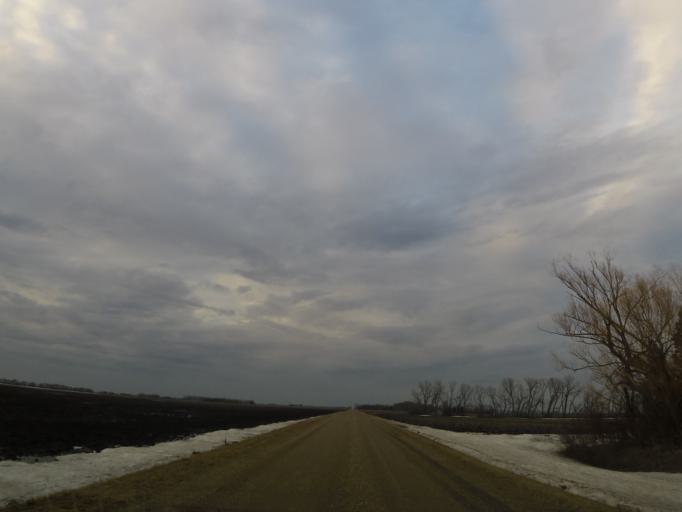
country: US
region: North Dakota
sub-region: Walsh County
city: Grafton
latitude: 48.3914
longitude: -97.2119
